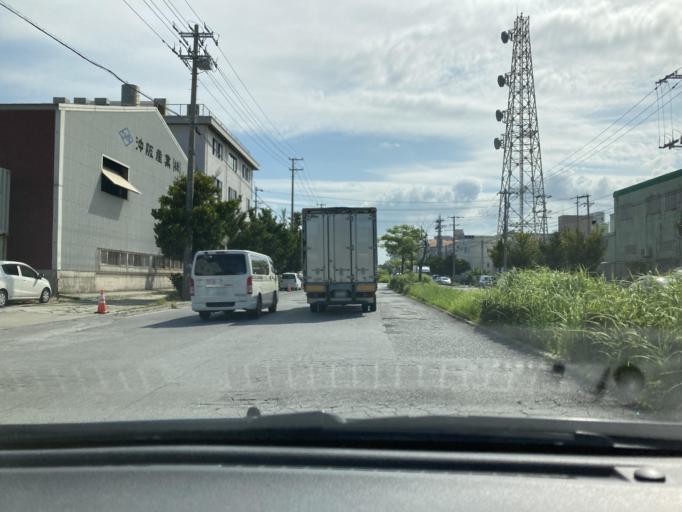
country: JP
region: Okinawa
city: Naha-shi
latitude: 26.2435
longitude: 127.6768
